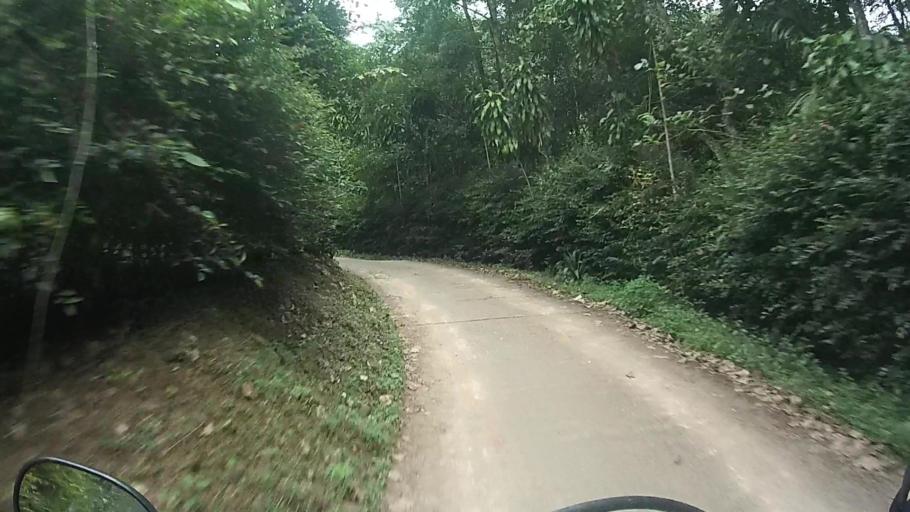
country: TH
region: Lampang
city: Mueang Pan
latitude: 18.8322
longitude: 99.3878
